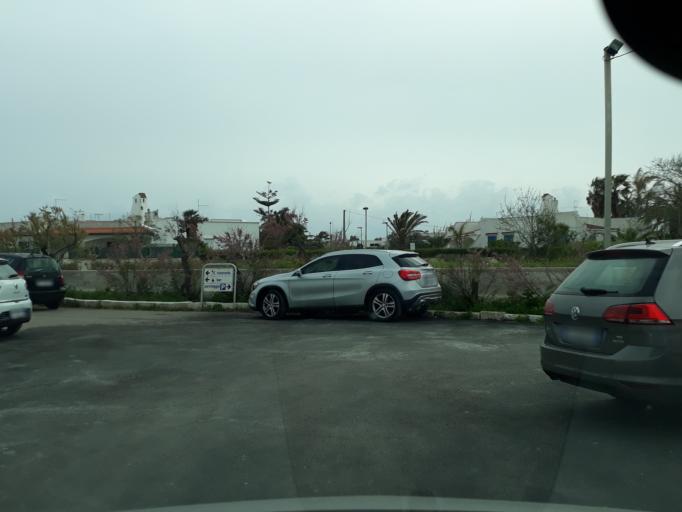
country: IT
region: Apulia
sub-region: Provincia di Brindisi
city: Ostuni
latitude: 40.7855
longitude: 17.6006
